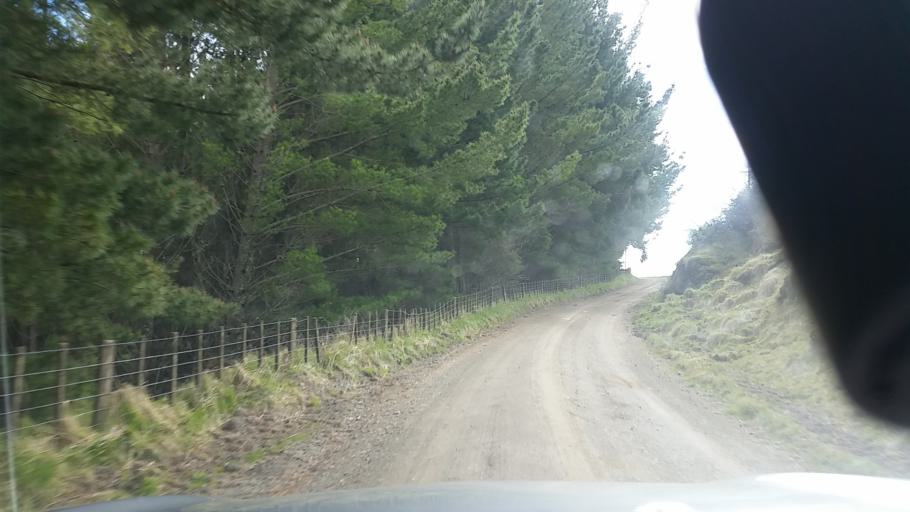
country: NZ
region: Hawke's Bay
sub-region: Napier City
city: Napier
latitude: -39.2173
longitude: 176.9827
